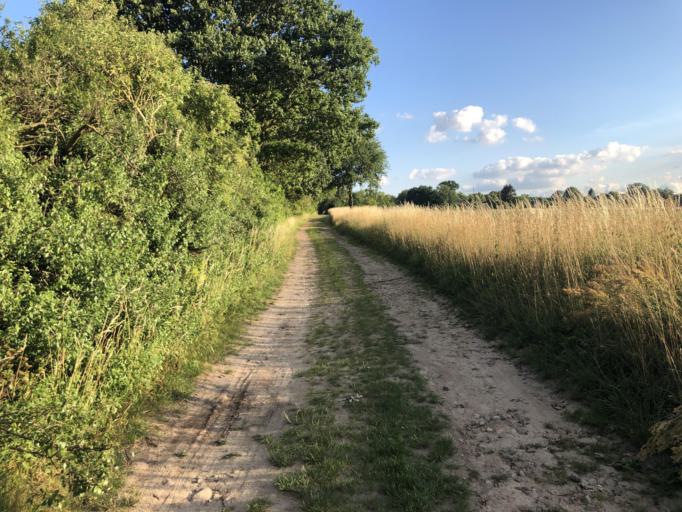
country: DE
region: Lower Saxony
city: Tosterglope
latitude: 53.2482
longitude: 10.7875
